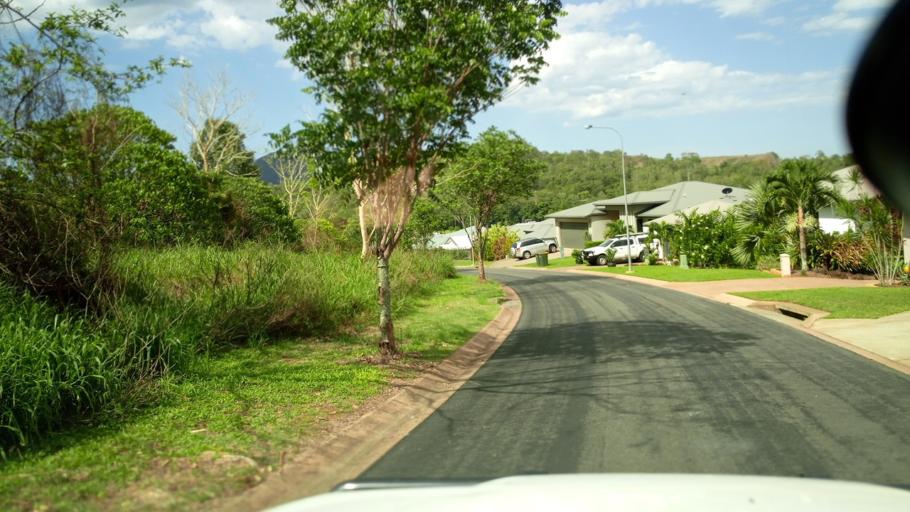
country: AU
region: Queensland
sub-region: Cairns
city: Woree
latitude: -16.9243
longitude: 145.7218
